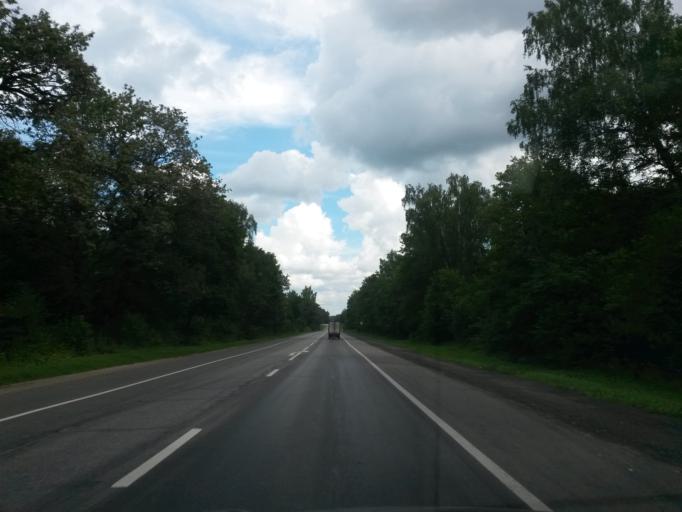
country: RU
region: Vladimir
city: Strunino
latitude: 56.5770
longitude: 38.5993
